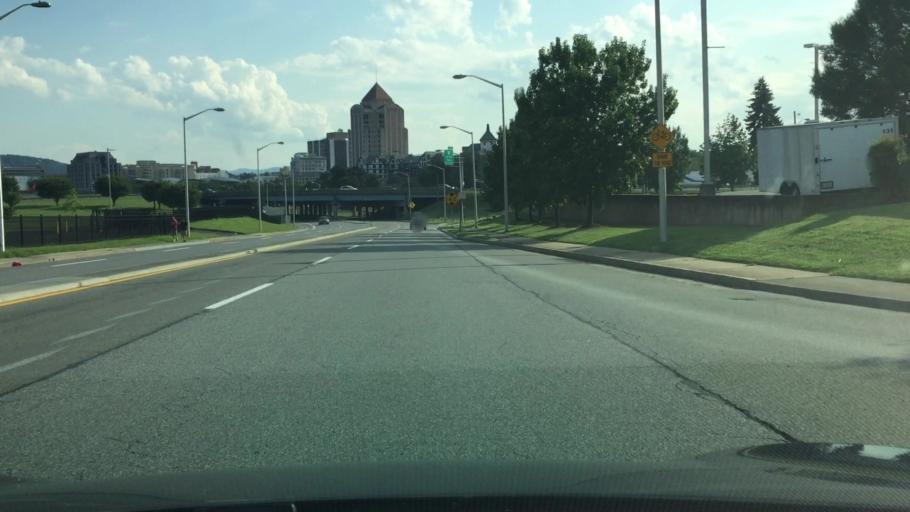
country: US
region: Virginia
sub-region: City of Roanoke
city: Roanoke
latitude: 37.2783
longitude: -79.9348
